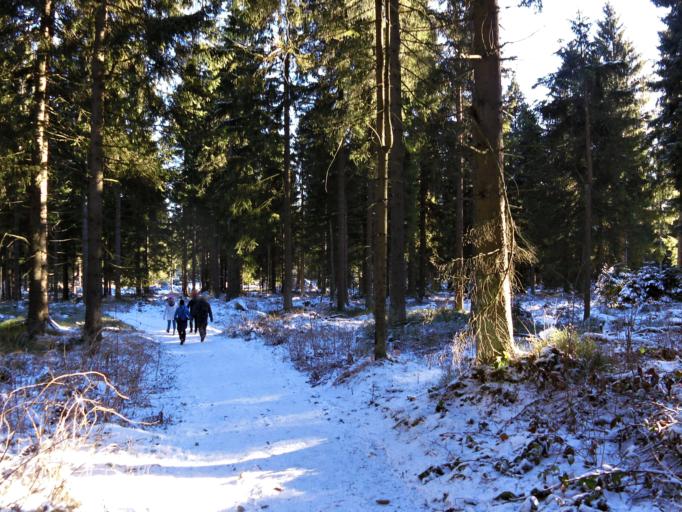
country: DE
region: Bavaria
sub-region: Upper Franconia
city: Fichtelberg
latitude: 50.0280
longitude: 11.8201
